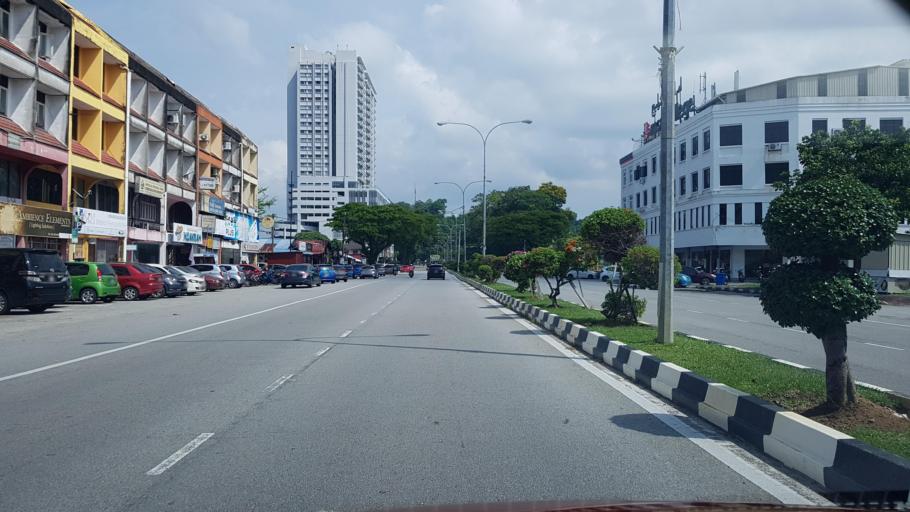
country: MY
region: Terengganu
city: Kuala Terengganu
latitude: 5.3250
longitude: 103.1416
